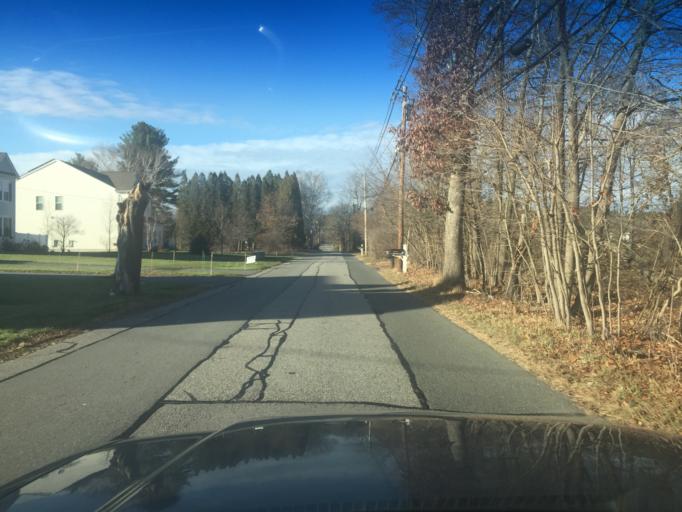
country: US
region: Massachusetts
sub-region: Middlesex County
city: Hopkinton
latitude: 42.2336
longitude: -71.4889
